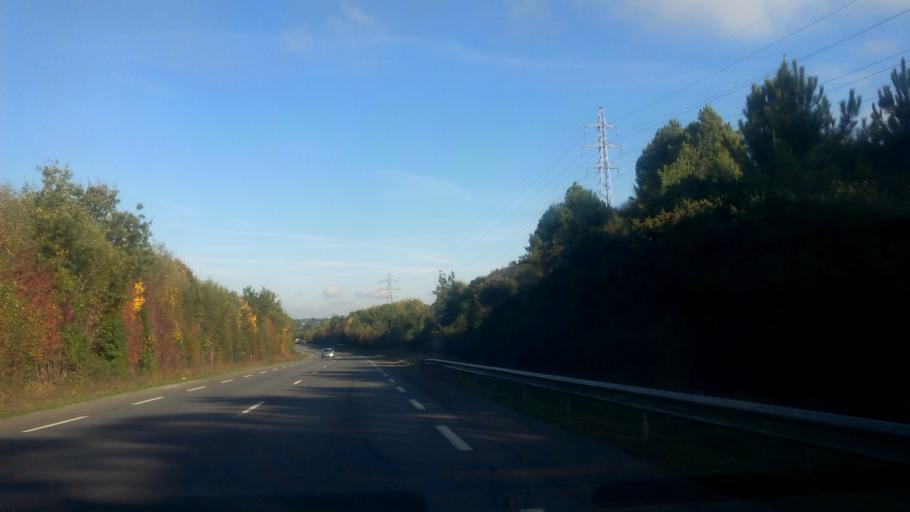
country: FR
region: Pays de la Loire
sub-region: Departement de la Loire-Atlantique
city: Saint-Nicolas-de-Redon
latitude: 47.6522
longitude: -2.0457
